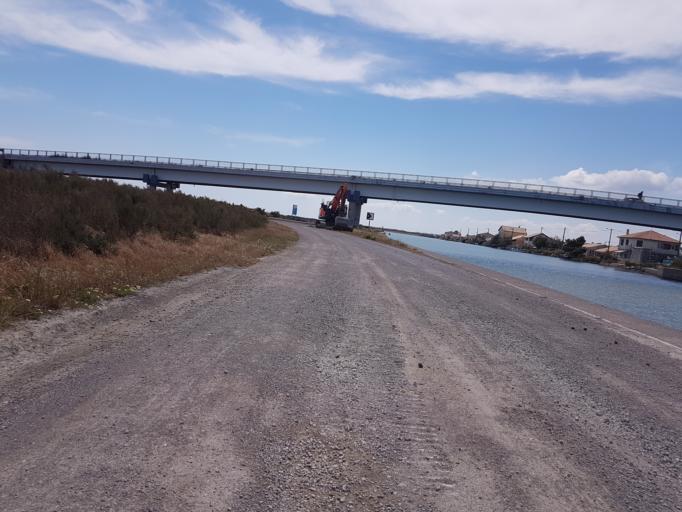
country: FR
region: Languedoc-Roussillon
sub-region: Departement de l'Herault
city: Vic-la-Gardiole
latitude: 43.4649
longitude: 3.8186
